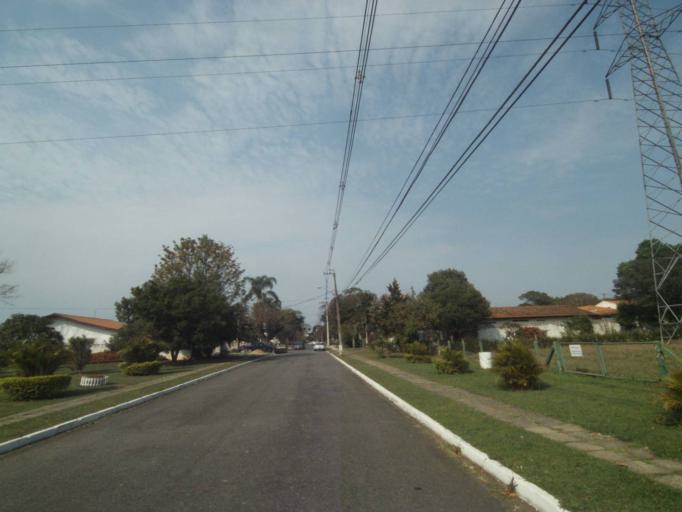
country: BR
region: Parana
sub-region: Pinhais
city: Pinhais
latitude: -25.4821
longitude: -49.2057
